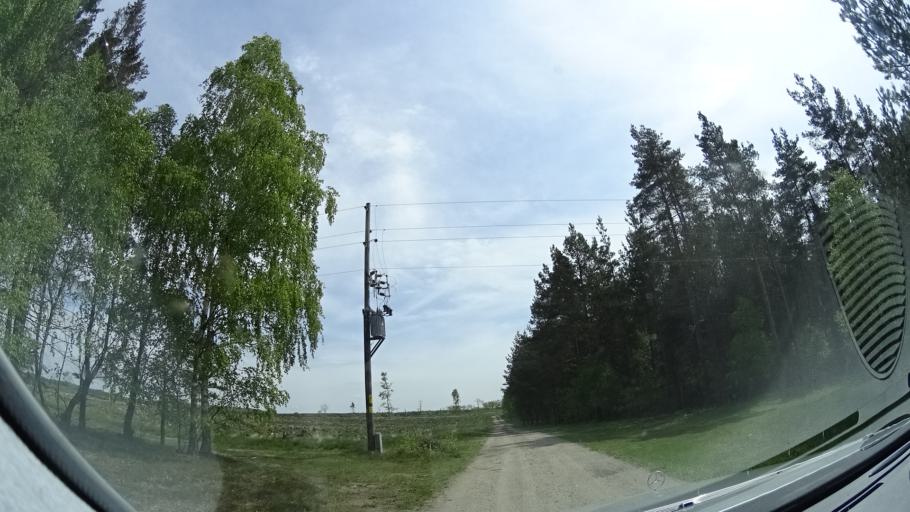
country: SE
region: Skane
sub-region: Sjobo Kommun
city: Sjoebo
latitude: 55.6675
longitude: 13.6494
